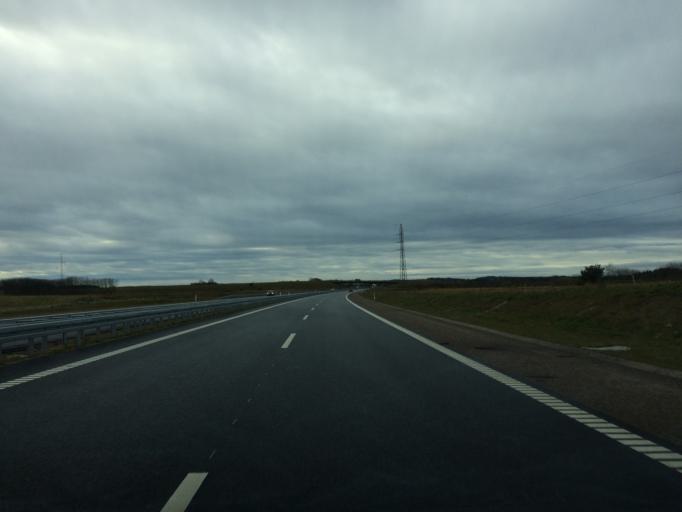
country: DK
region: Central Jutland
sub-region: Silkeborg Kommune
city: Silkeborg
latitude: 56.1512
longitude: 9.4519
